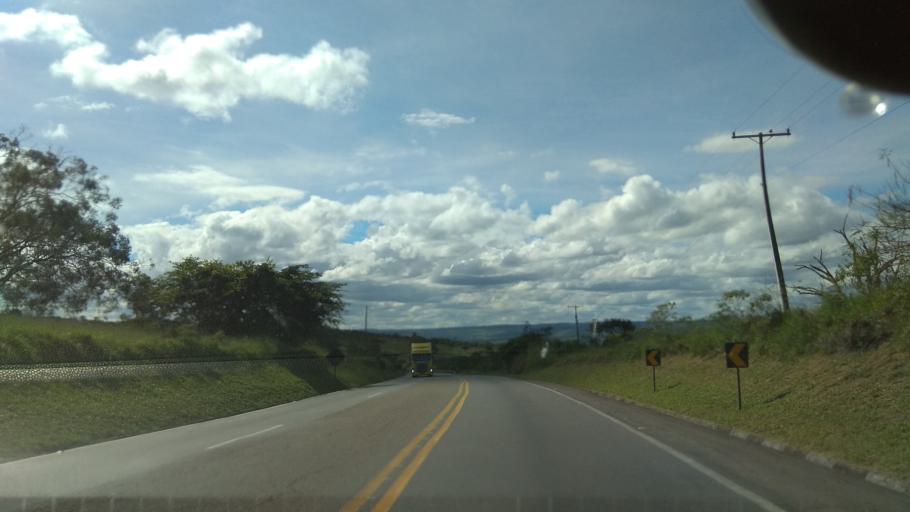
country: BR
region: Bahia
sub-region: Santa Ines
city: Santa Ines
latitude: -13.1988
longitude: -40.0109
